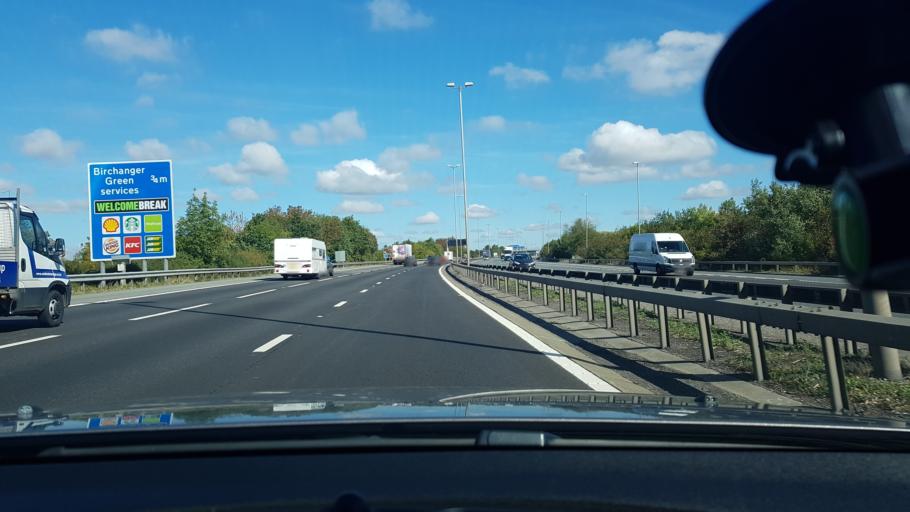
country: GB
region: England
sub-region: Essex
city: Little Hallingbury
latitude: 51.8559
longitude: 0.1857
